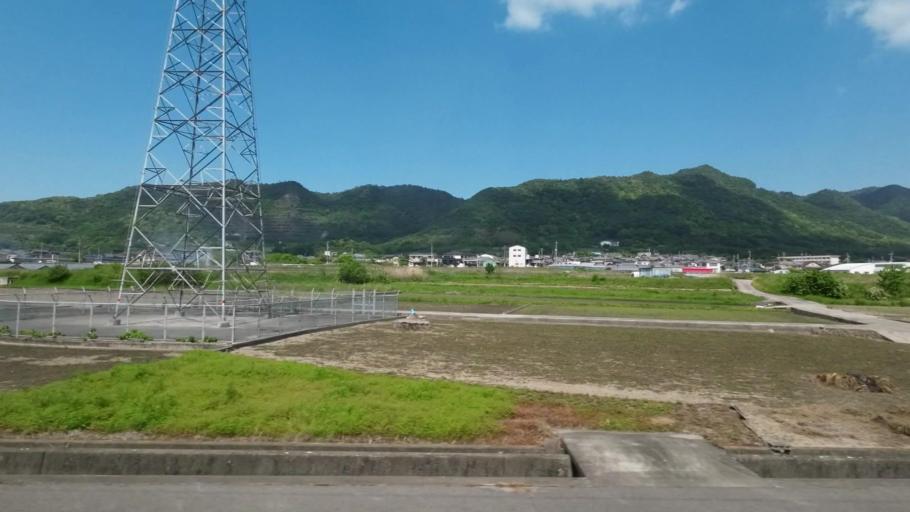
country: JP
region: Kagawa
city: Kan'onjicho
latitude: 34.1498
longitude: 133.6870
